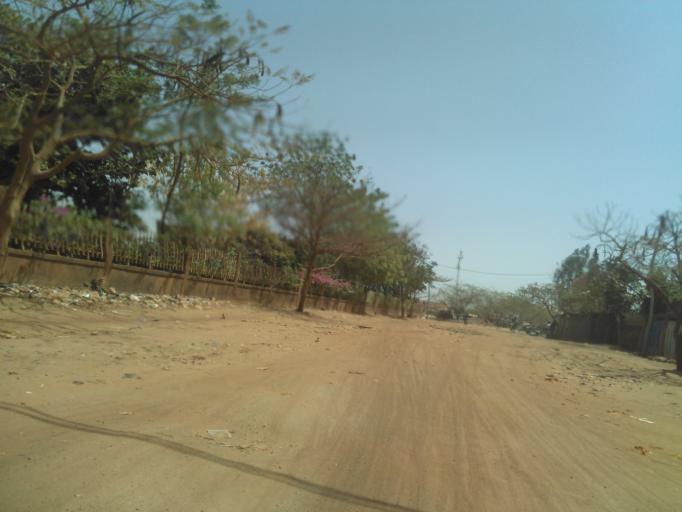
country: BF
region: Centre
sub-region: Kadiogo Province
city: Ouagadougou
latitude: 12.3923
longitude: -1.5690
